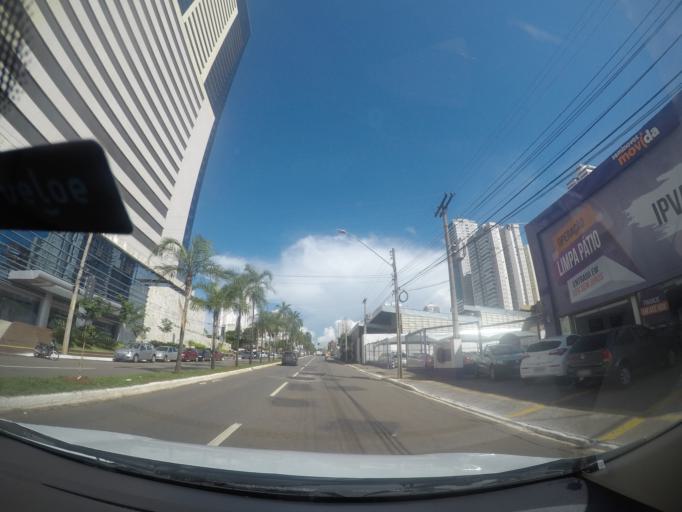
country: BR
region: Goias
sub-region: Goiania
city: Goiania
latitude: -16.6969
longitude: -49.2703
